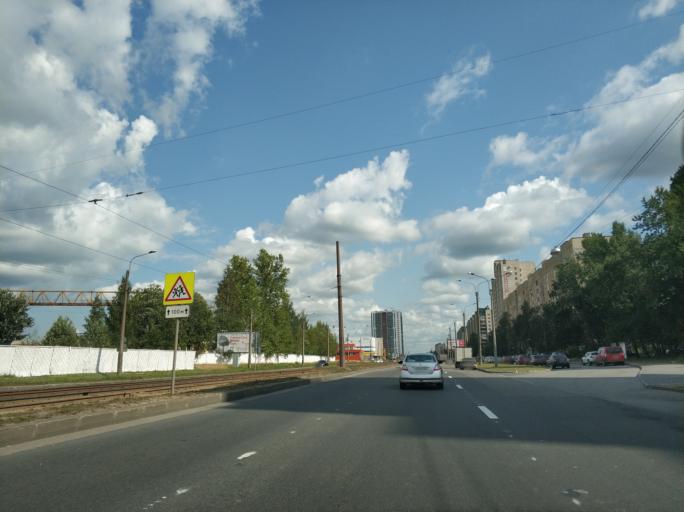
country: RU
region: St.-Petersburg
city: Krasnogvargeisky
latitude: 59.9562
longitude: 30.4683
